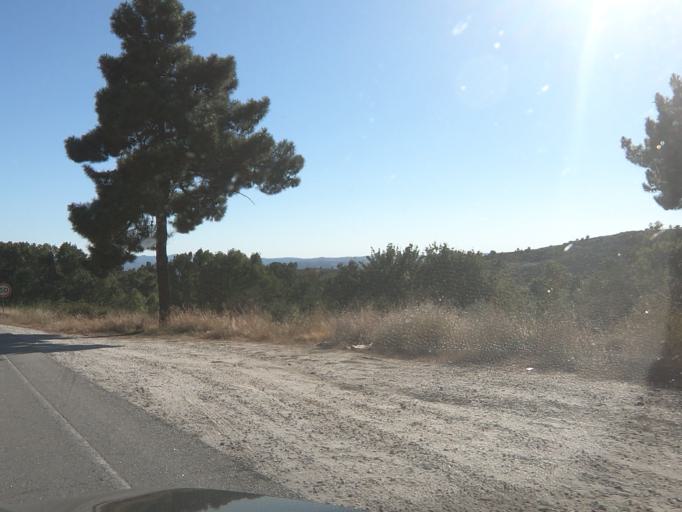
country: PT
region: Vila Real
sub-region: Valpacos
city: Valpacos
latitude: 41.6330
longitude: -7.3180
